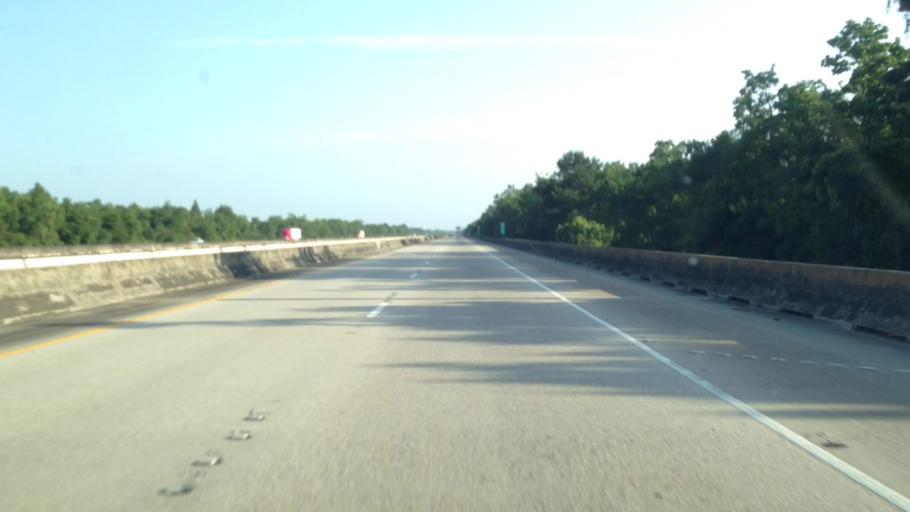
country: US
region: Louisiana
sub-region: Tangipahoa Parish
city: Ponchatoula
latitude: 30.3740
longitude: -90.4230
